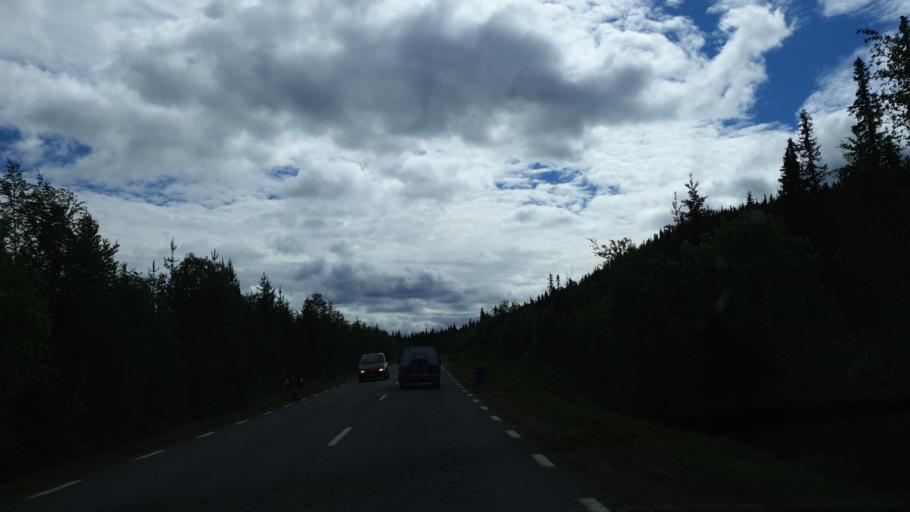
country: SE
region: Vaesterbotten
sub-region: Vilhelmina Kommun
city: Sjoberg
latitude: 64.8877
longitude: 15.8633
